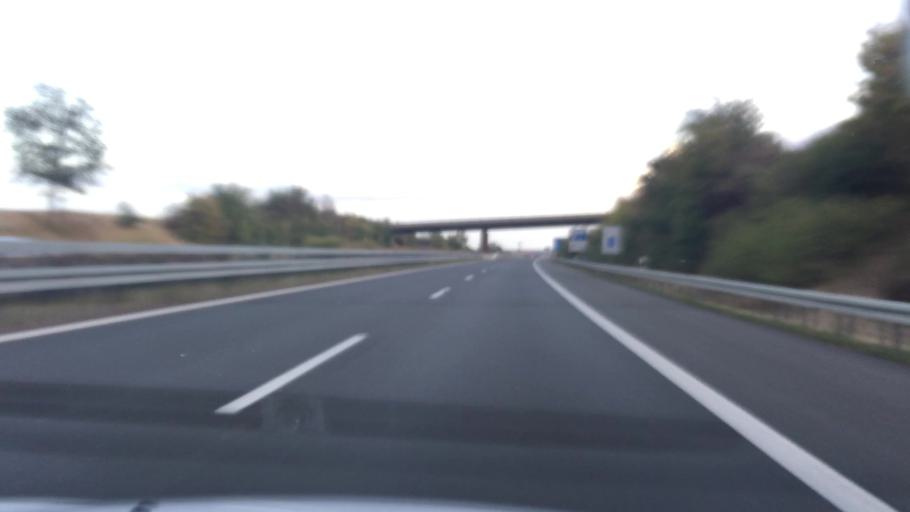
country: DE
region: Saxony-Anhalt
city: Oppin
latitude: 51.5519
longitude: 12.0082
